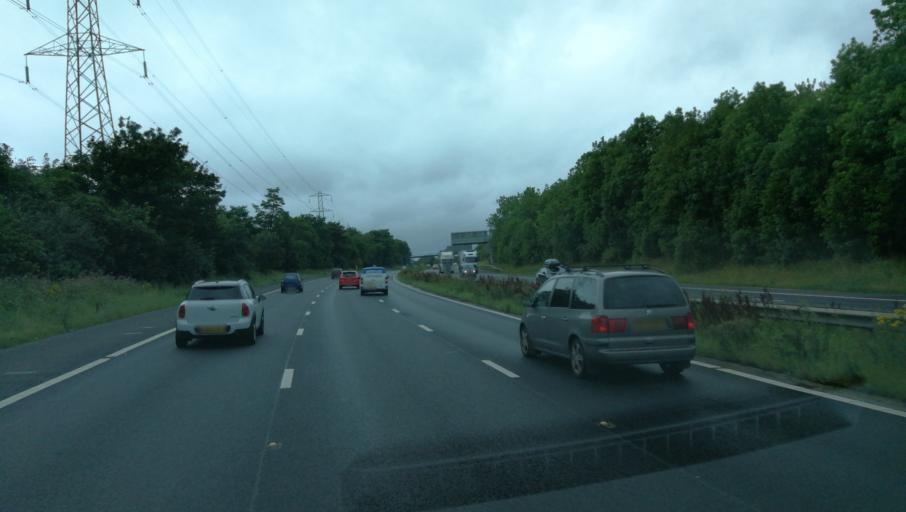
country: GB
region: England
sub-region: City and Borough of Salford
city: Little Hulton
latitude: 53.5388
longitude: -2.4120
